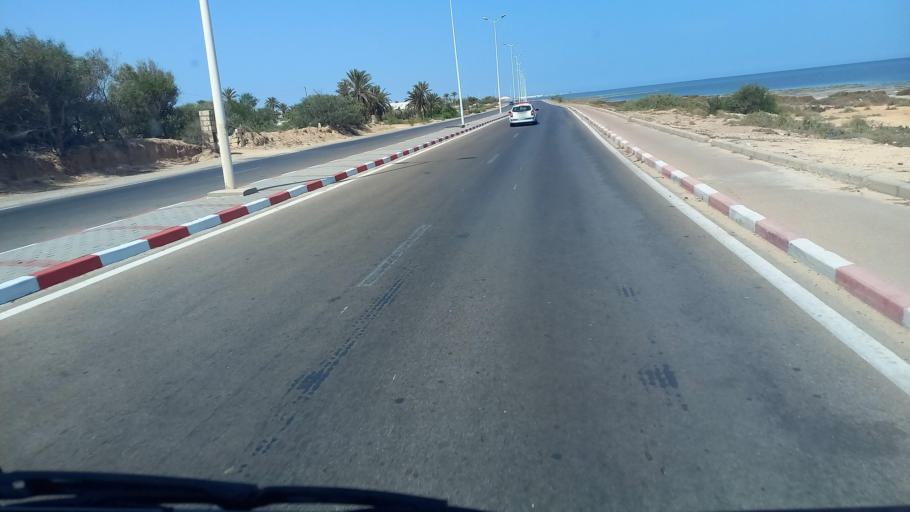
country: TN
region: Madanin
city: Houmt Souk
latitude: 33.8736
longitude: 10.9083
